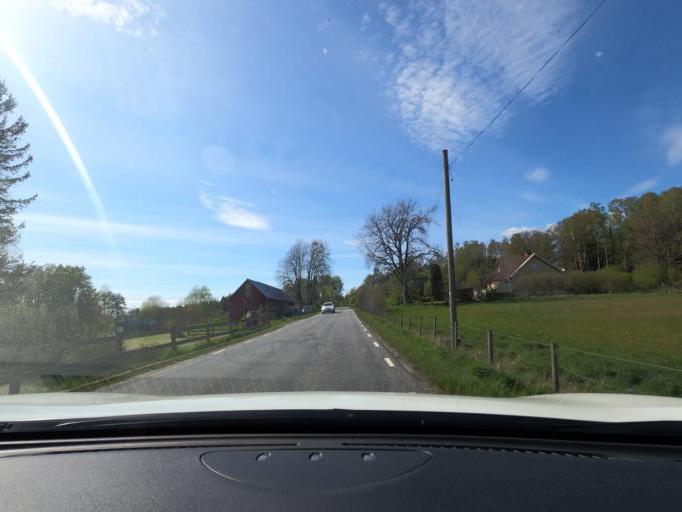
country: SE
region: Vaestra Goetaland
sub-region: Marks Kommun
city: Kinna
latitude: 57.4761
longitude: 12.5734
